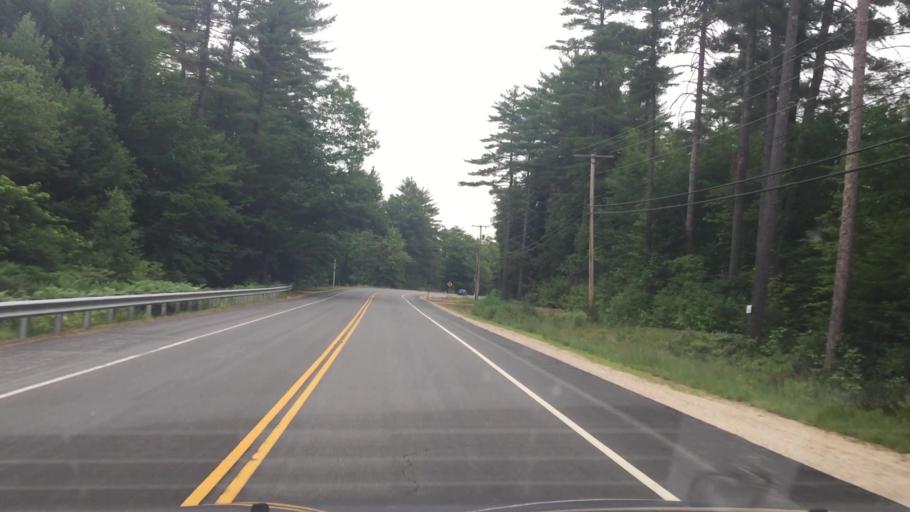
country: US
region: New Hampshire
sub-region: Carroll County
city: Tamworth
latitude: 43.8423
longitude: -71.2651
